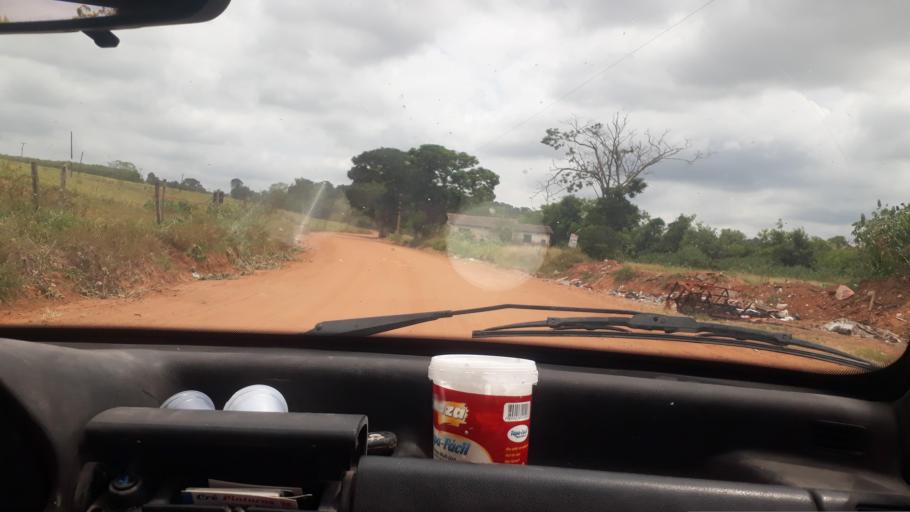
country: BR
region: Sao Paulo
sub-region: Regente Feijo
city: Regente Feijo
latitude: -22.2402
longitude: -51.2977
